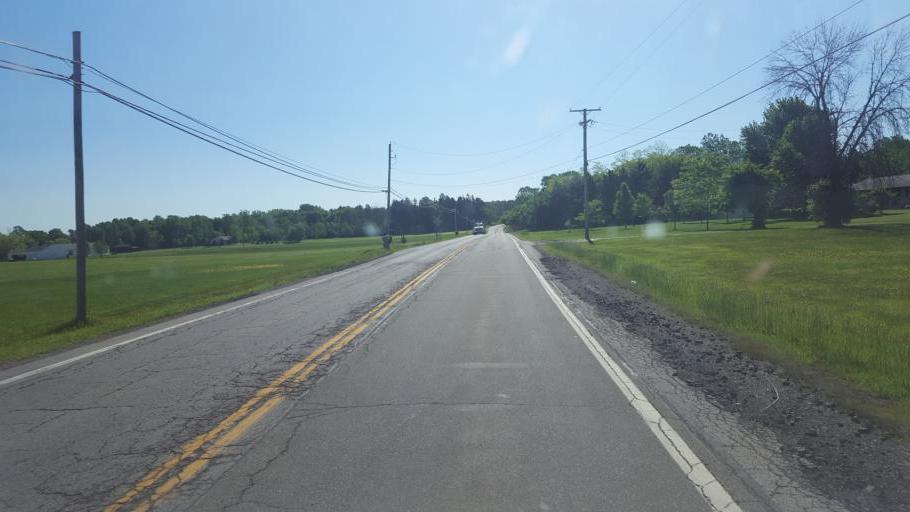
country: US
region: Ohio
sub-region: Crawford County
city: Crestline
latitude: 40.7666
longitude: -82.6743
